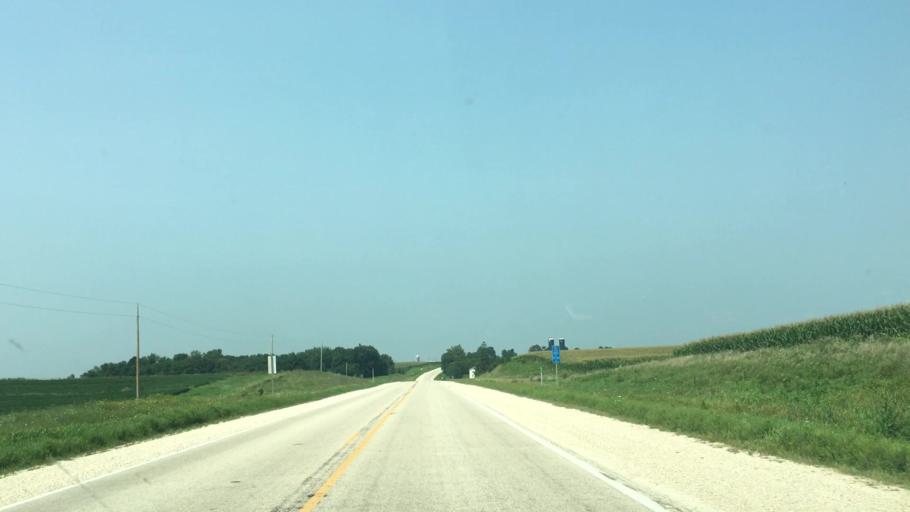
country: US
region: Iowa
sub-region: Fayette County
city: West Union
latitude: 42.9992
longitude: -91.8241
